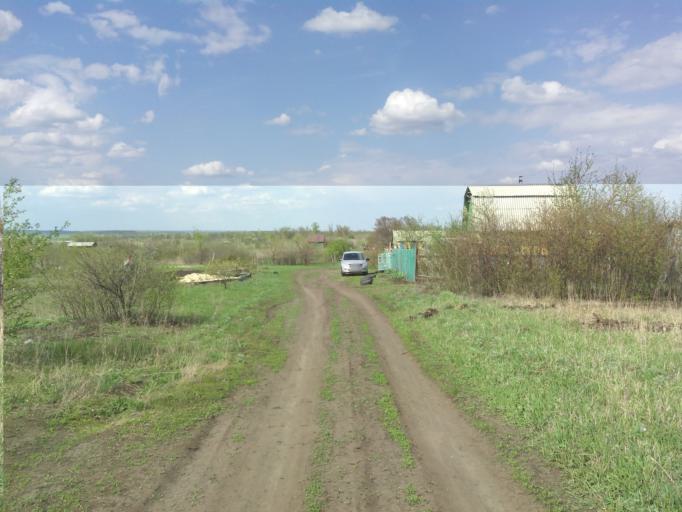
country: RU
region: Voronezj
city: Borisoglebsk
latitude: 51.3743
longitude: 42.1487
